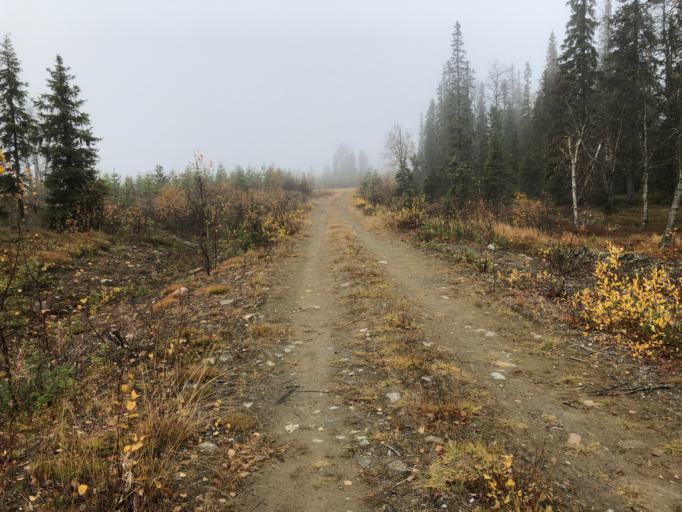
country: FI
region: Northern Ostrobothnia
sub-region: Koillismaa
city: Kuusamo
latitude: 66.5874
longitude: 29.3477
